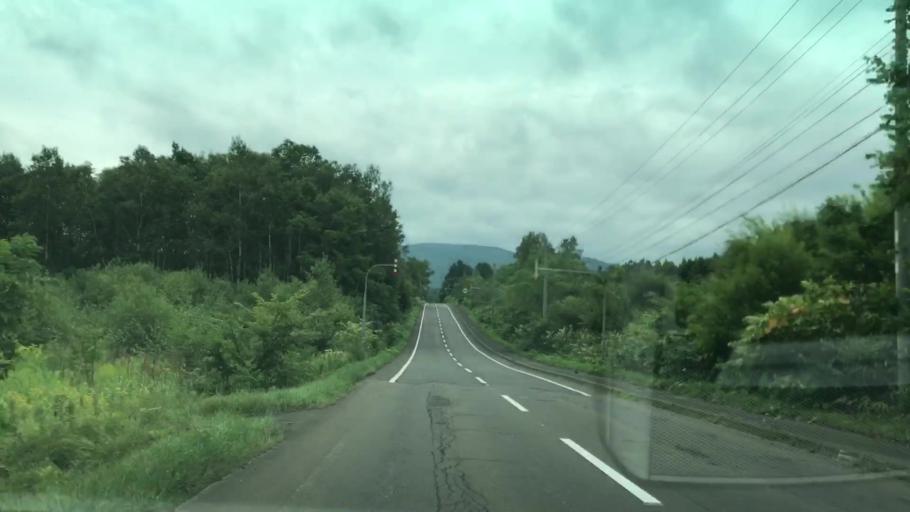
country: JP
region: Hokkaido
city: Yoichi
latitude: 43.0701
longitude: 140.8180
